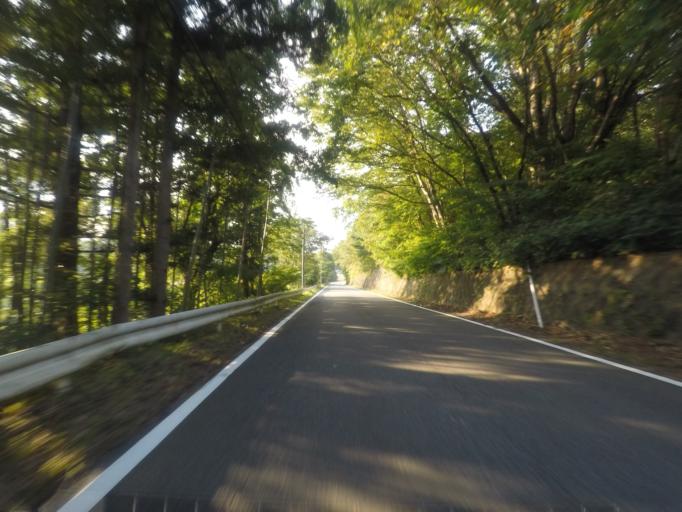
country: JP
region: Fukushima
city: Namie
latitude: 37.5642
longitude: 140.8040
